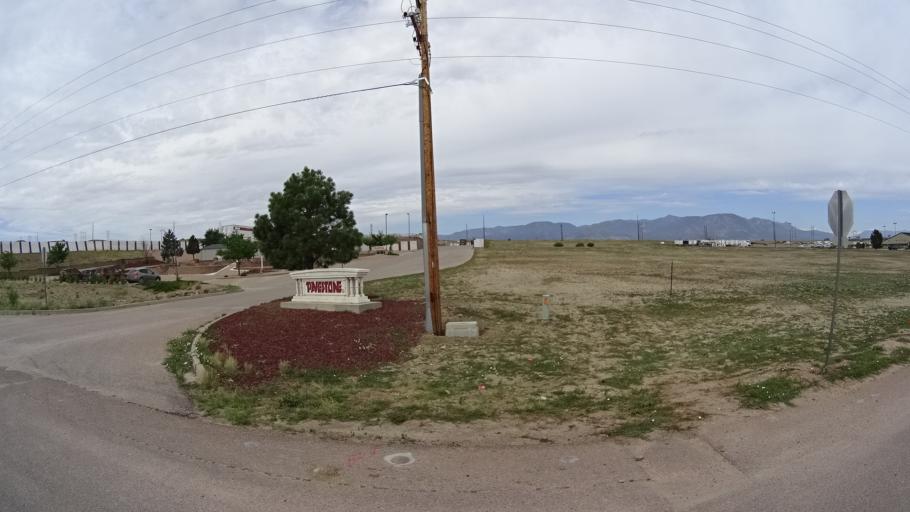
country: US
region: Colorado
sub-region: El Paso County
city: Fountain
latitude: 38.6717
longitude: -104.7149
